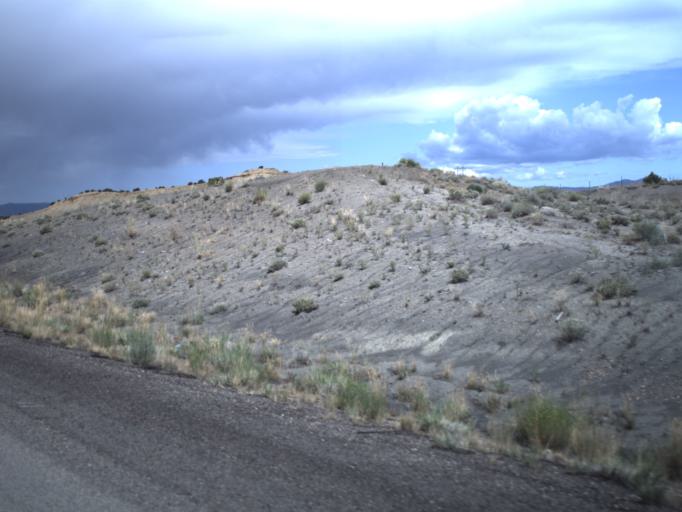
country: US
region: Utah
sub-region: Carbon County
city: Wellington
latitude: 39.5470
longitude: -110.6362
